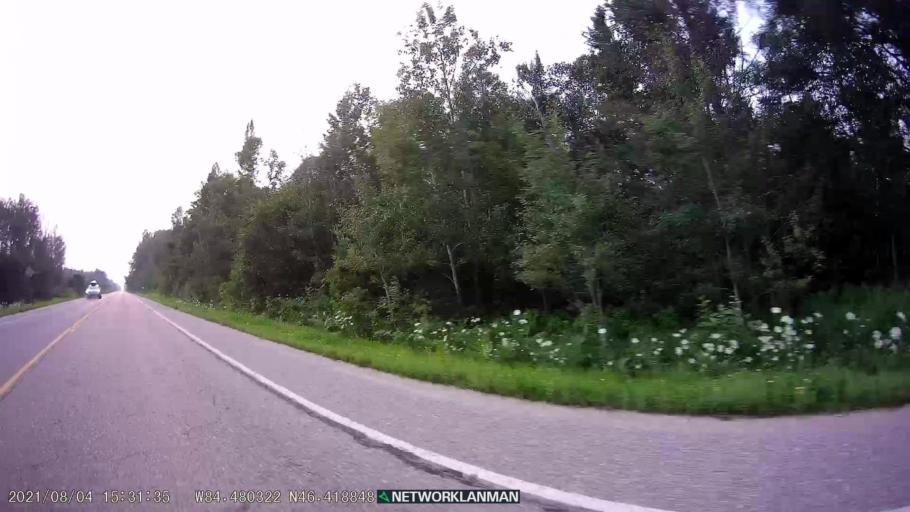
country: US
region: Michigan
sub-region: Chippewa County
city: Sault Ste. Marie
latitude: 46.4189
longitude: -84.4809
